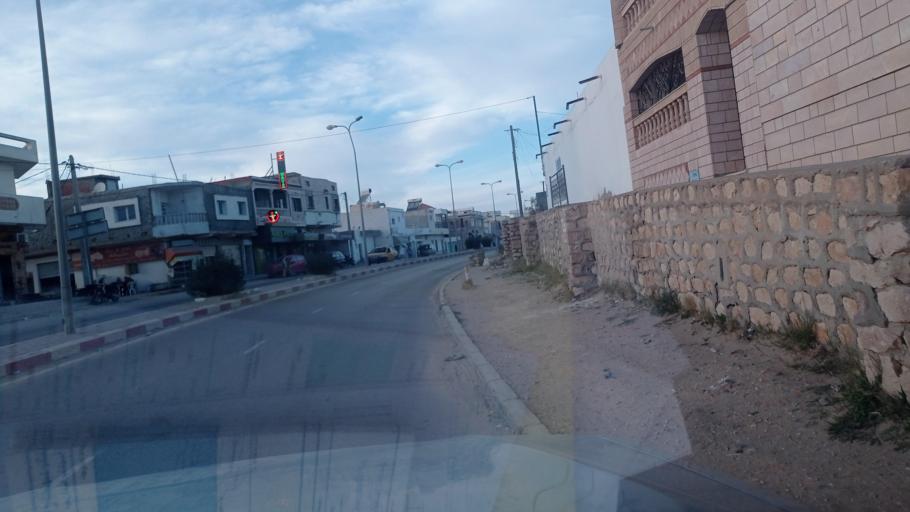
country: TN
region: Qabis
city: Gabes
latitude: 33.8413
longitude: 10.1142
